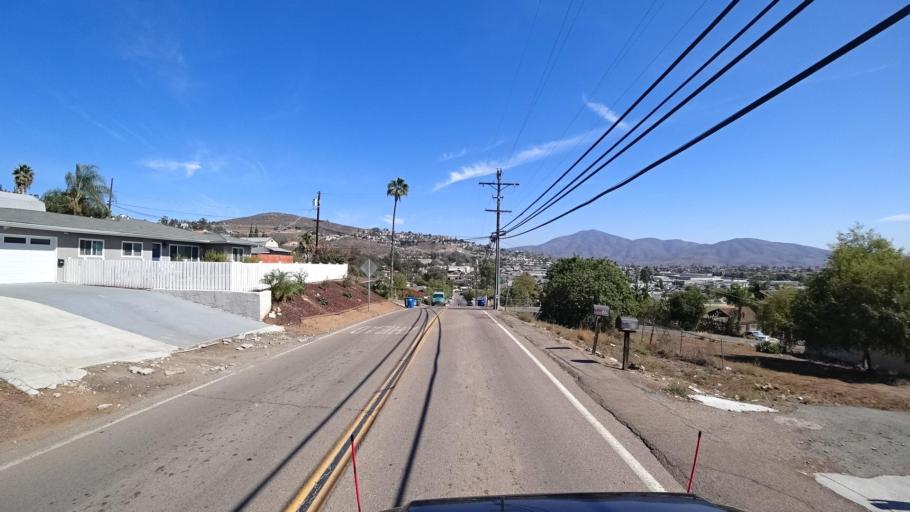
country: US
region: California
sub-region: San Diego County
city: La Presa
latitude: 32.7190
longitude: -117.0087
